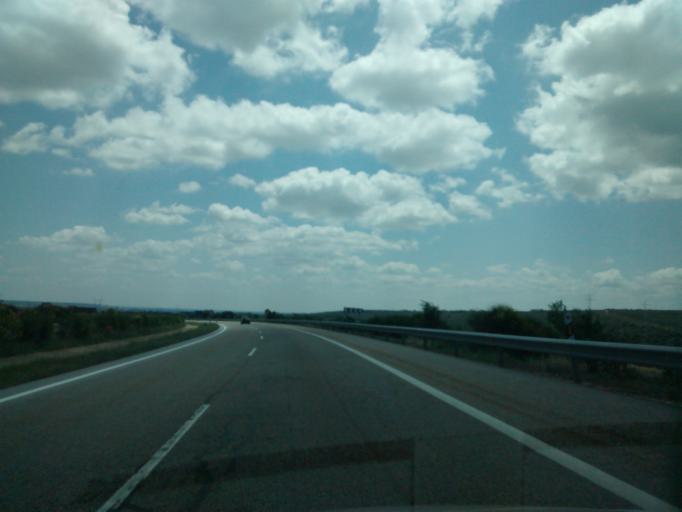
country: ES
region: Castille and Leon
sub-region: Provincia de Leon
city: Brazuelo
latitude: 42.4871
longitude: -6.1250
